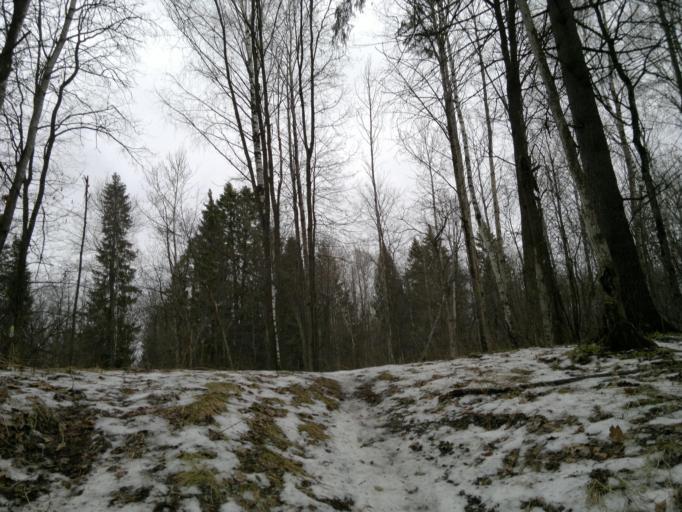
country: RU
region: Mariy-El
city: Yoshkar-Ola
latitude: 56.6120
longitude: 47.9354
